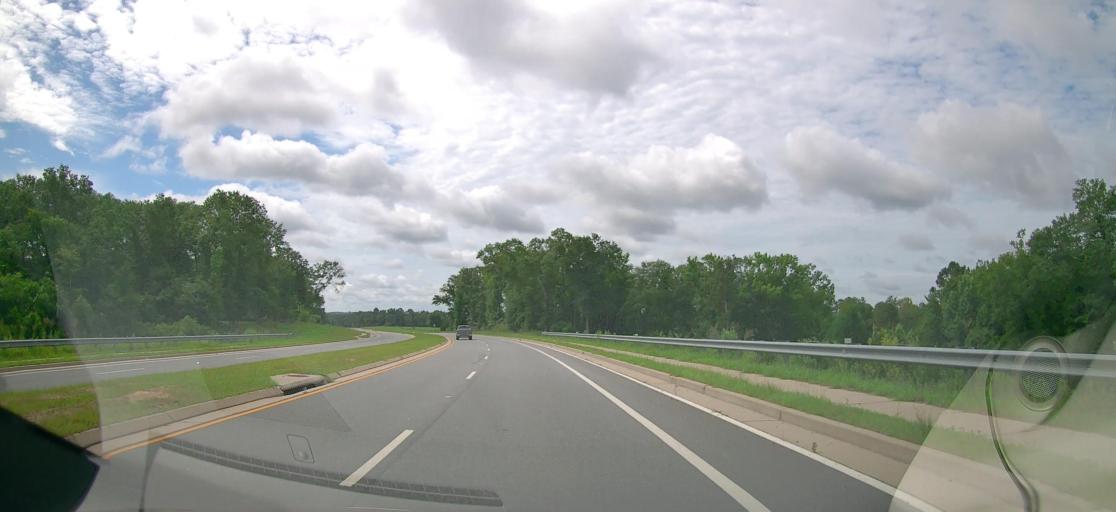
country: US
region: Georgia
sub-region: Houston County
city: Centerville
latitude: 32.7013
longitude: -83.6946
